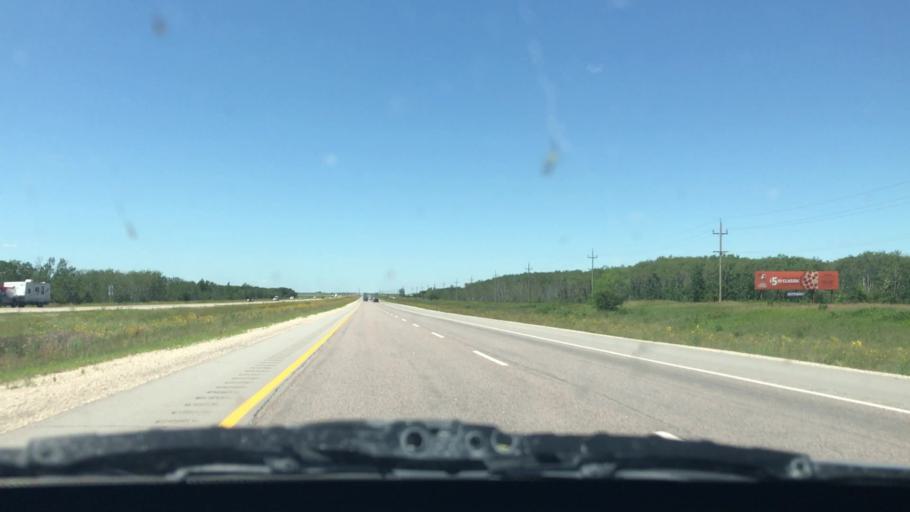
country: CA
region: Manitoba
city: Steinbach
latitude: 49.6828
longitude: -96.5998
